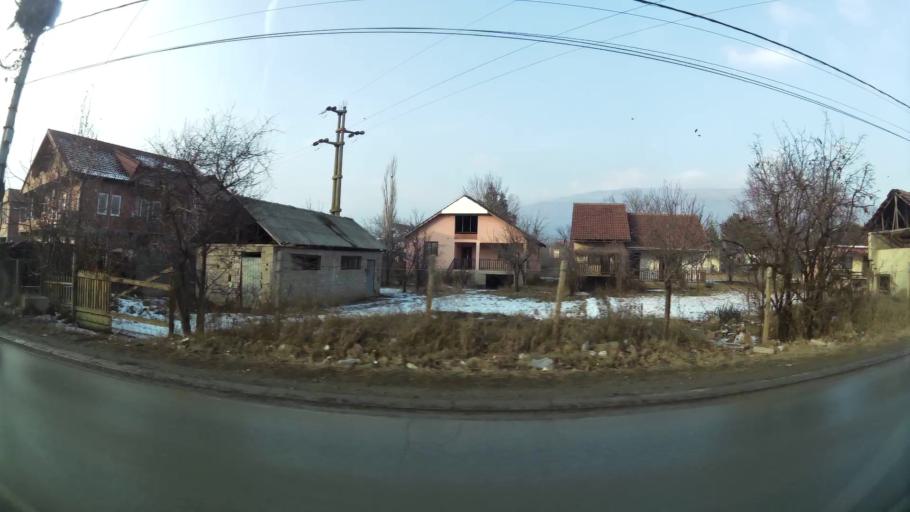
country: MK
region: Aracinovo
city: Arachinovo
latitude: 42.0238
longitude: 21.5524
